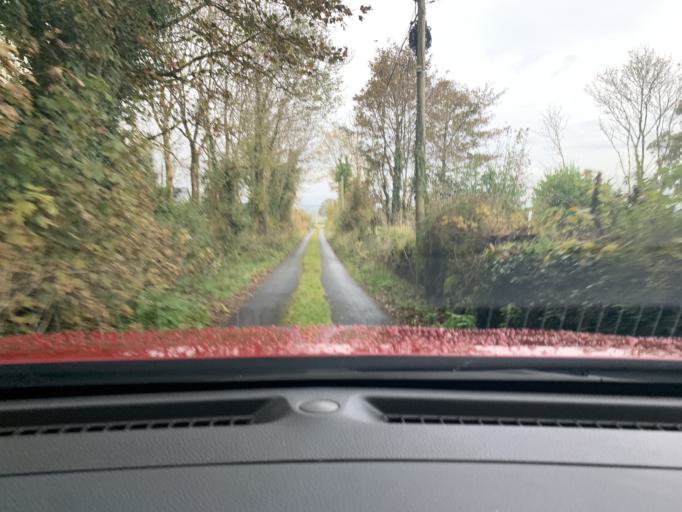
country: IE
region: Connaught
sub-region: Roscommon
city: Ballaghaderreen
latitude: 53.9175
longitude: -8.5562
